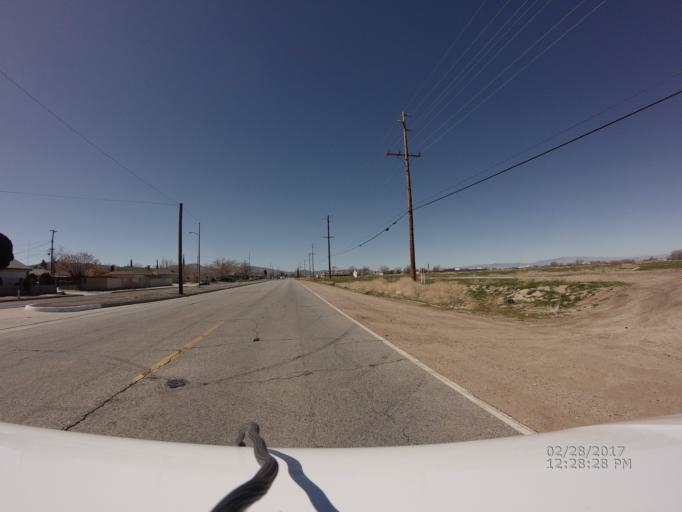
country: US
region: California
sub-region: Los Angeles County
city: Palmdale
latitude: 34.5875
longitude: -118.0704
